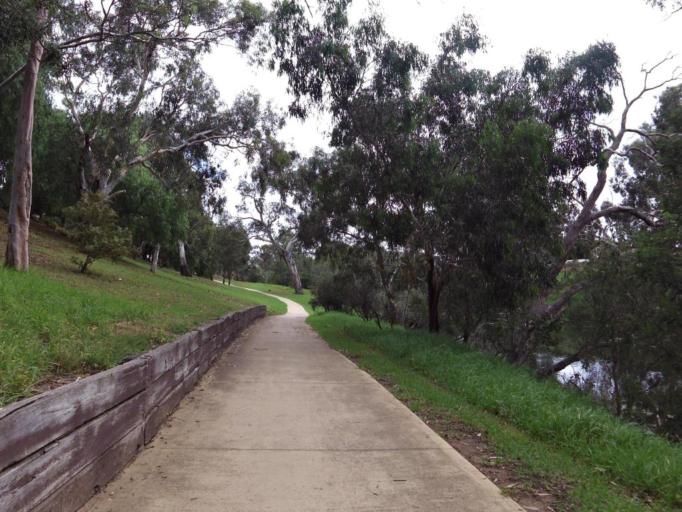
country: AU
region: Victoria
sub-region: Wyndham
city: Werribee
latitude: -37.8921
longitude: 144.6467
